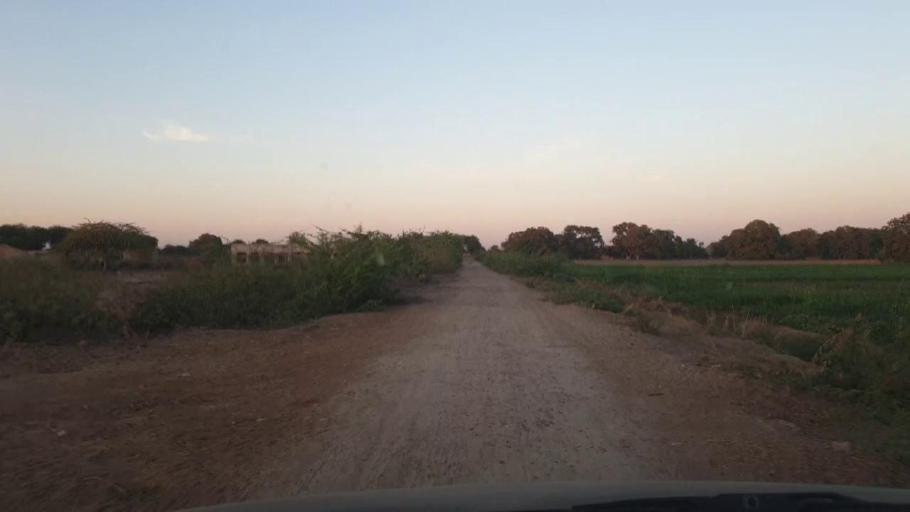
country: PK
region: Sindh
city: Umarkot
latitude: 25.3749
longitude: 69.7089
